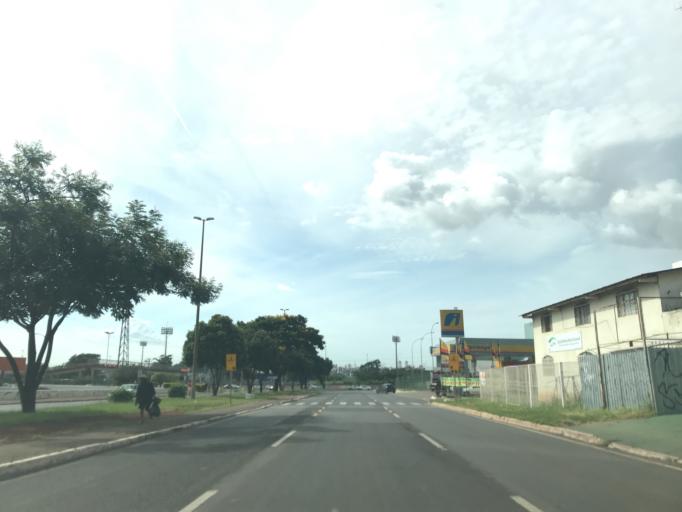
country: BR
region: Federal District
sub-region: Brasilia
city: Brasilia
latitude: -15.8327
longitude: -48.0825
